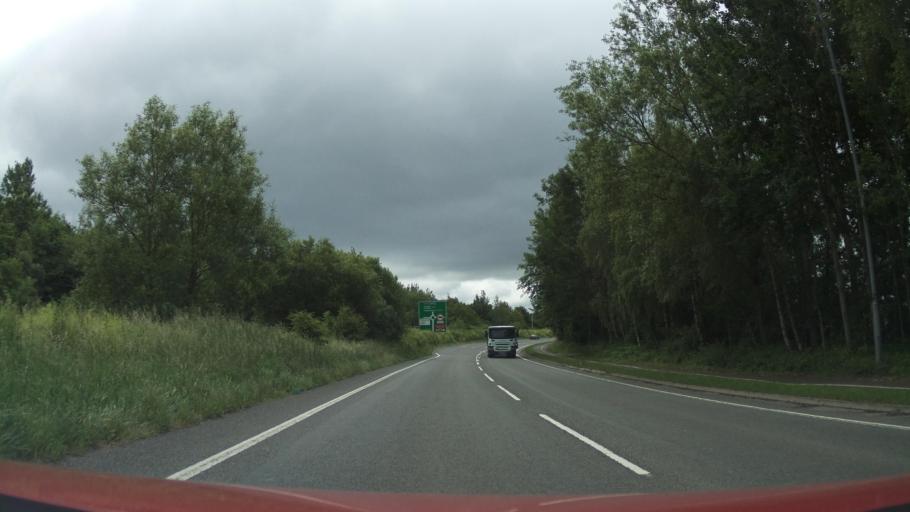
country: GB
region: England
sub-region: Leicestershire
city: Ashby de la Zouch
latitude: 52.7545
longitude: -1.4516
